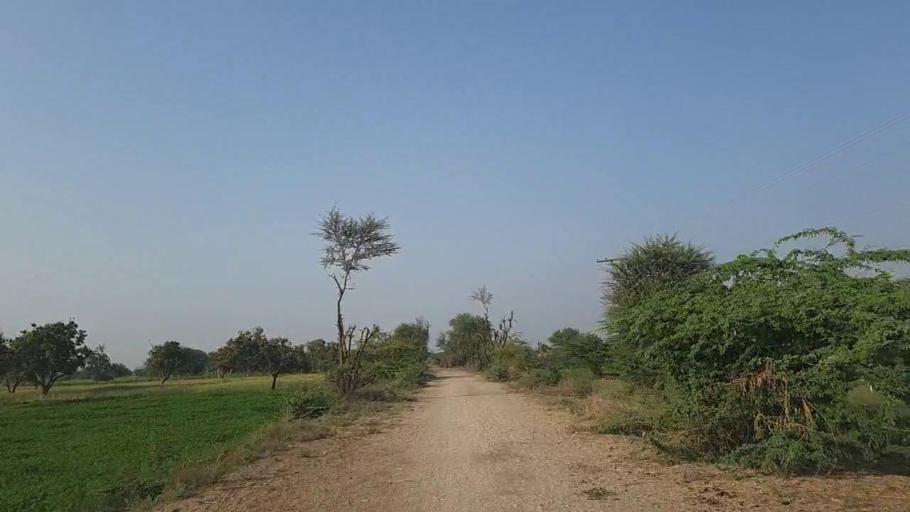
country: PK
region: Sindh
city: Dhoro Naro
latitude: 25.4947
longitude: 69.4997
